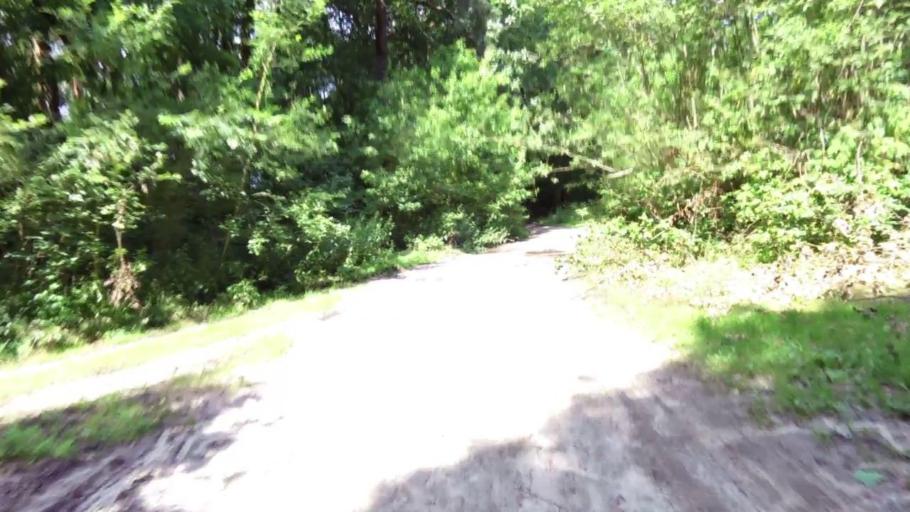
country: PL
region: West Pomeranian Voivodeship
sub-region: Powiat gryfinski
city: Stare Czarnowo
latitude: 53.3545
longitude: 14.7538
